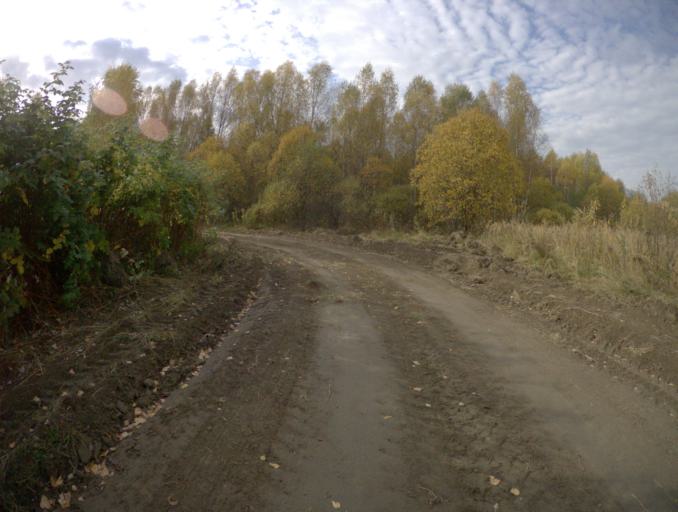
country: RU
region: Vladimir
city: Golovino
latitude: 55.9824
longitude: 40.3973
